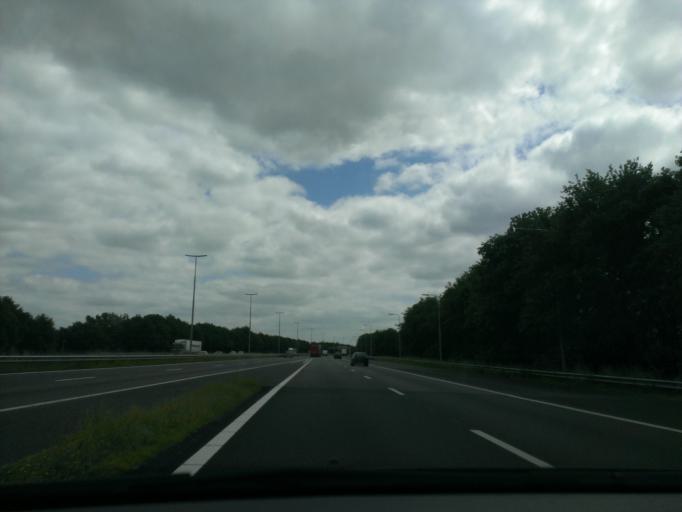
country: NL
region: Gelderland
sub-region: Gemeente Hattem
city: Hattem
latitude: 52.4824
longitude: 6.0288
